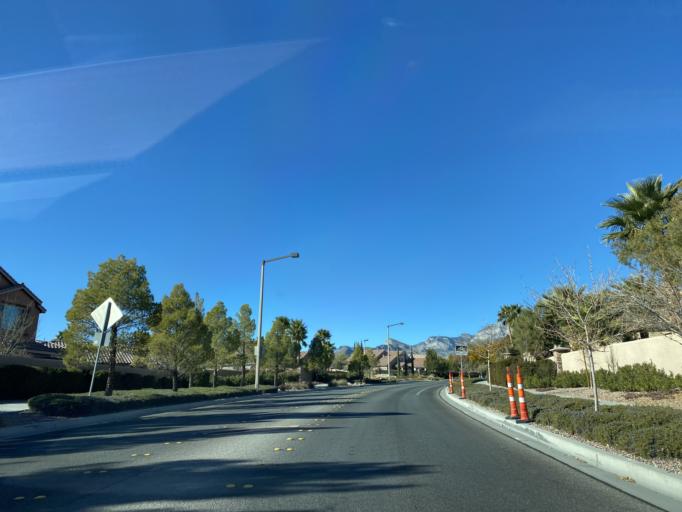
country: US
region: Nevada
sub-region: Clark County
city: Summerlin South
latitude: 36.1616
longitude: -115.3466
